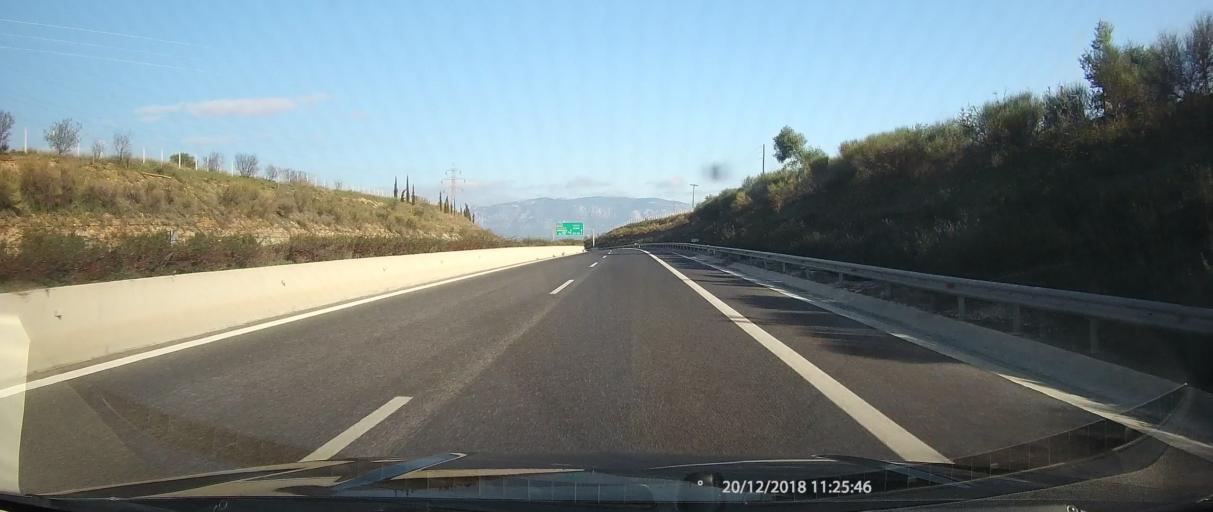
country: GR
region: Peloponnese
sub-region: Nomos Korinthias
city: Arkhaia Korinthos
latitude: 37.9041
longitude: 22.9042
